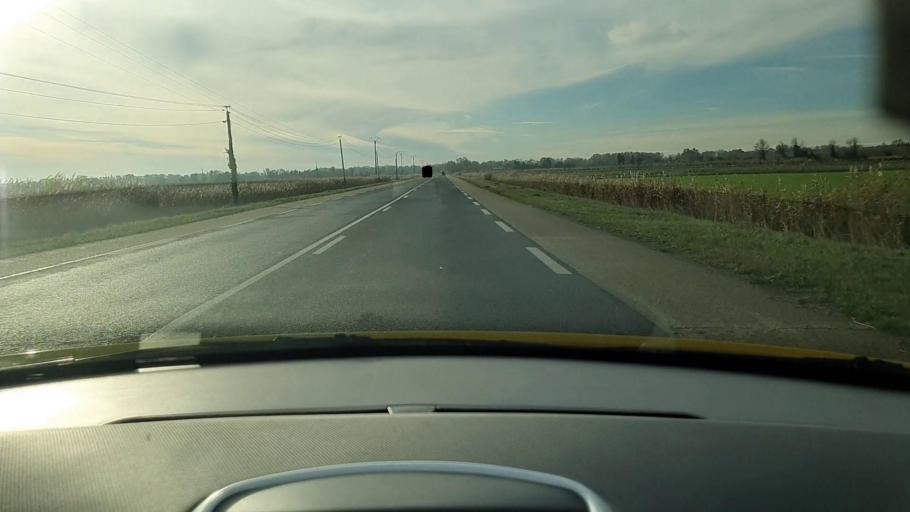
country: FR
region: Languedoc-Roussillon
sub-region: Departement du Gard
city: Bellegarde
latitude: 43.7192
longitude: 4.5482
